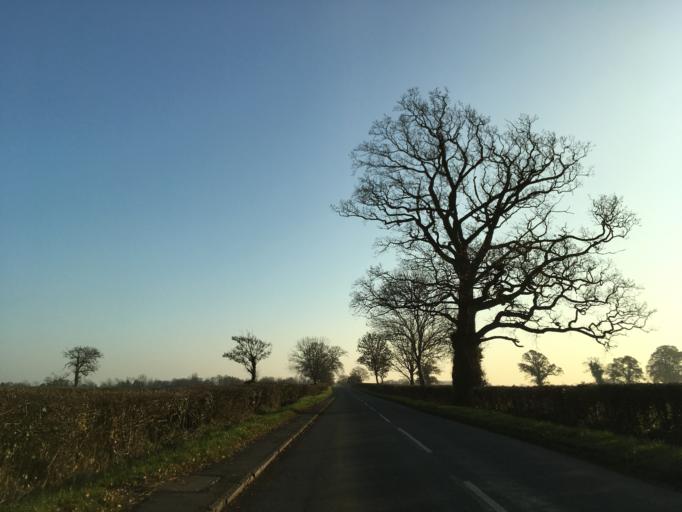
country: GB
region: England
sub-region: Wiltshire
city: Nettleton
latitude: 51.5360
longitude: -2.2811
